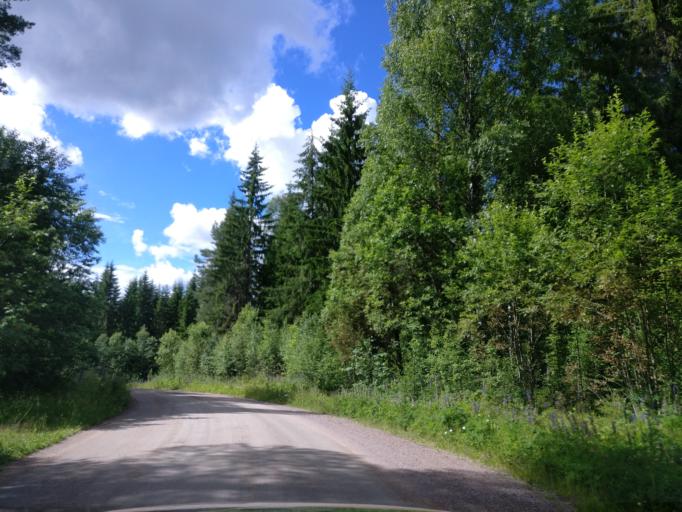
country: SE
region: Vaermland
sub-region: Hagfors Kommun
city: Hagfors
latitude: 60.0432
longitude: 13.6613
